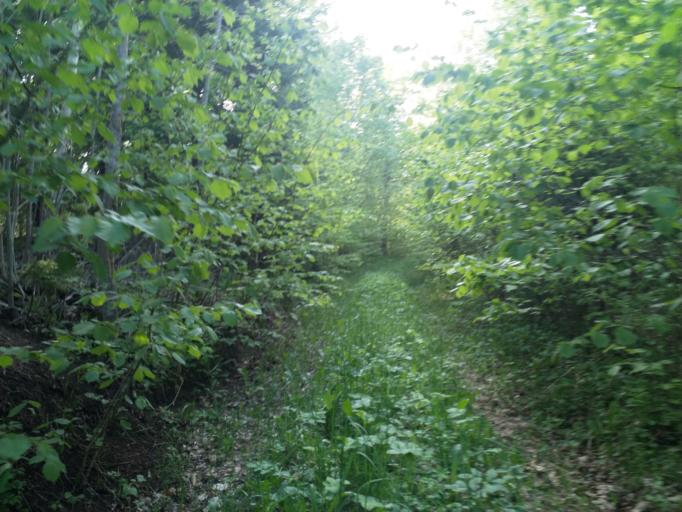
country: LV
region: Kuldigas Rajons
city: Kuldiga
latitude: 56.8565
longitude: 21.8650
